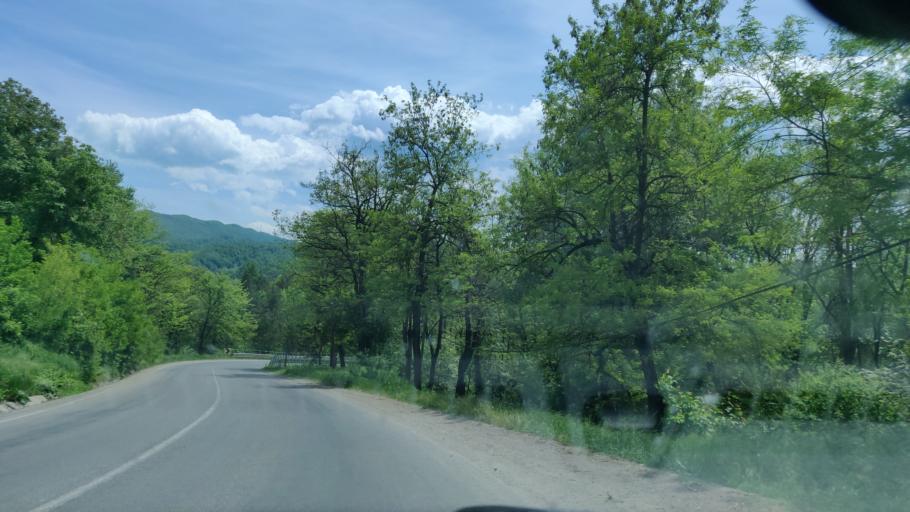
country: RO
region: Vrancea
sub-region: Comuna Vidra
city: Vidra
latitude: 45.9061
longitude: 26.8923
